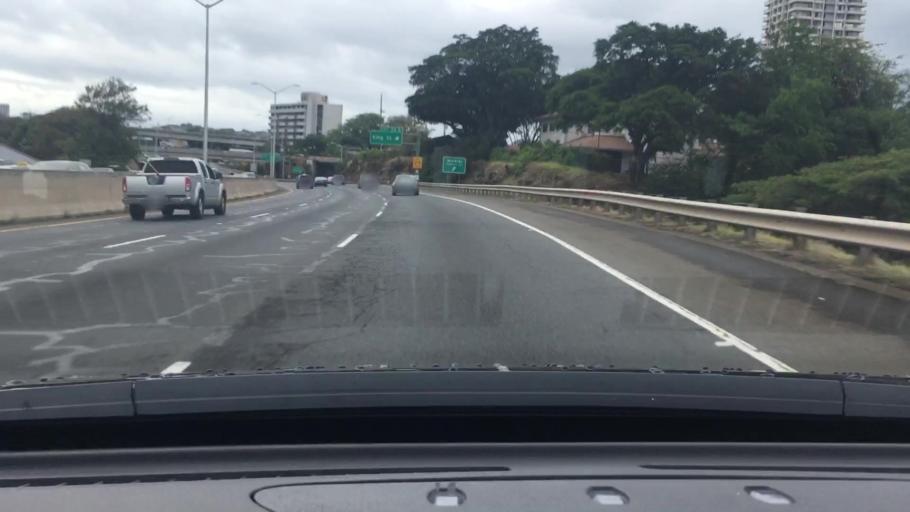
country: US
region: Hawaii
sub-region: Honolulu County
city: Honolulu
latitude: 21.2921
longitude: -157.8192
